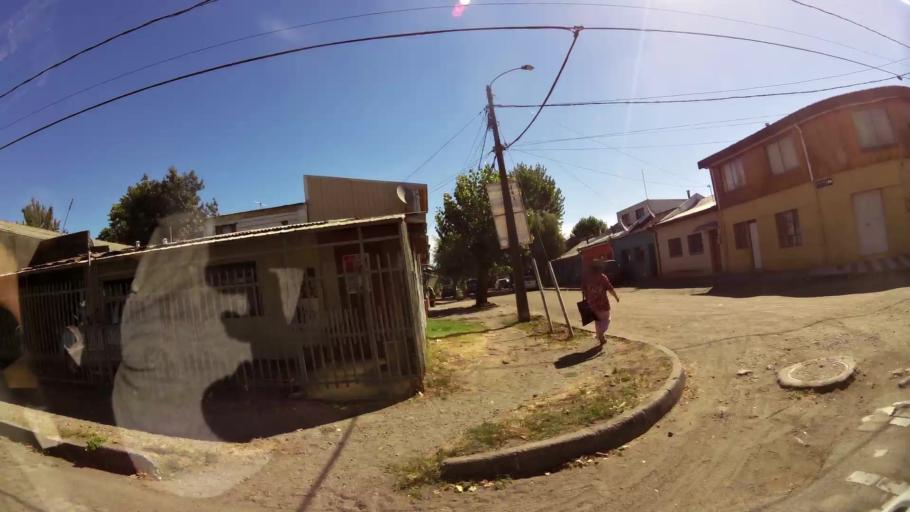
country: CL
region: Biobio
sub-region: Provincia de Concepcion
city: Concepcion
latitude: -36.8339
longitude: -73.0584
